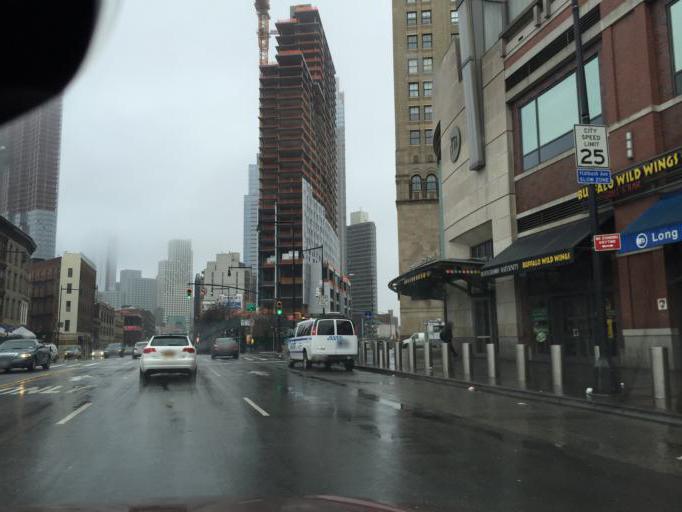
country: US
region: New York
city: New York City
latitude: 40.6845
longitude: -73.9777
